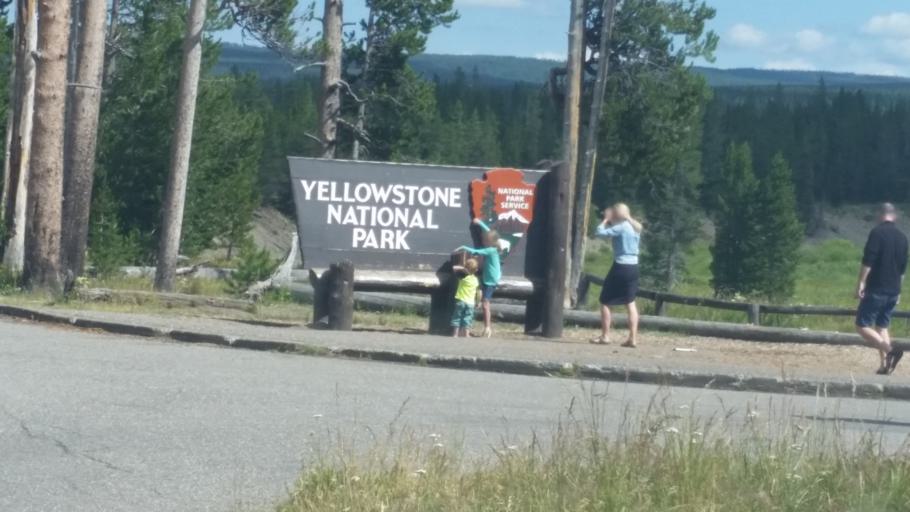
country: US
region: Idaho
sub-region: Teton County
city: Driggs
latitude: 44.1330
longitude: -110.6649
